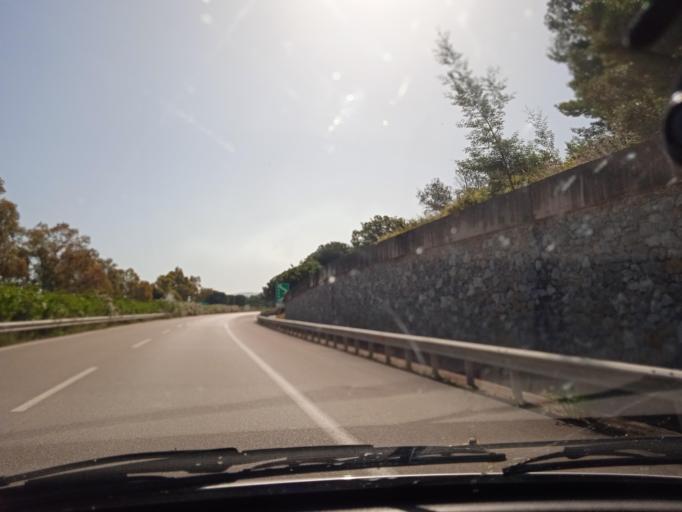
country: IT
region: Sicily
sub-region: Messina
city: Acquedolci
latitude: 38.0491
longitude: 14.5678
